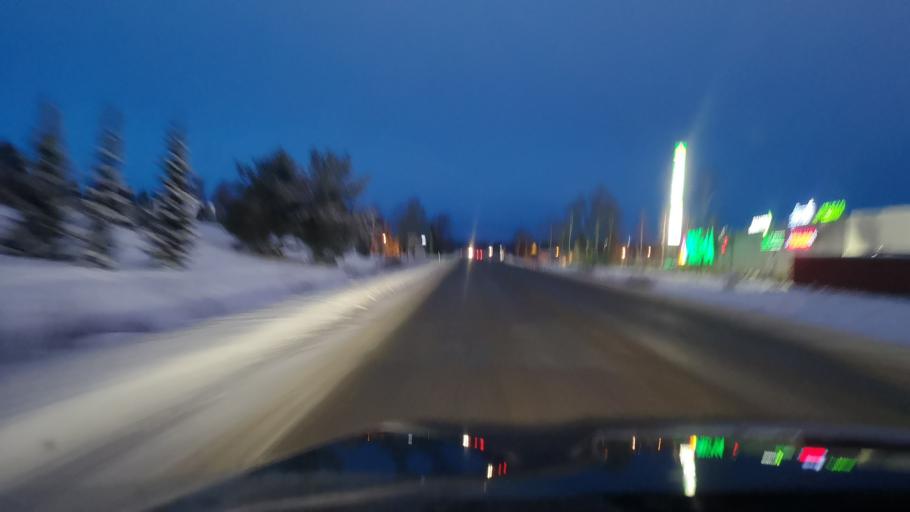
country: FI
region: Varsinais-Suomi
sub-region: Loimaa
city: Loimaa
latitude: 60.8564
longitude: 23.0418
